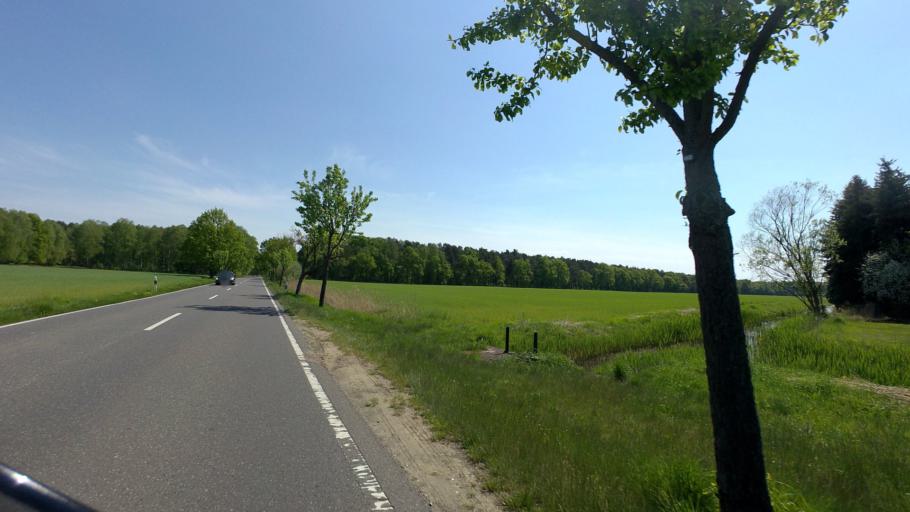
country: DE
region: Brandenburg
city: Schlepzig
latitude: 52.0705
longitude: 13.8978
